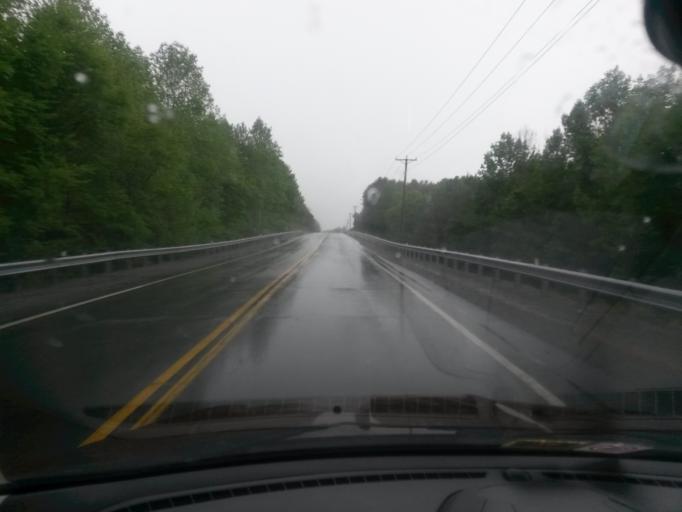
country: US
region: Virginia
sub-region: Floyd County
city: Floyd
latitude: 36.9808
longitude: -80.4032
